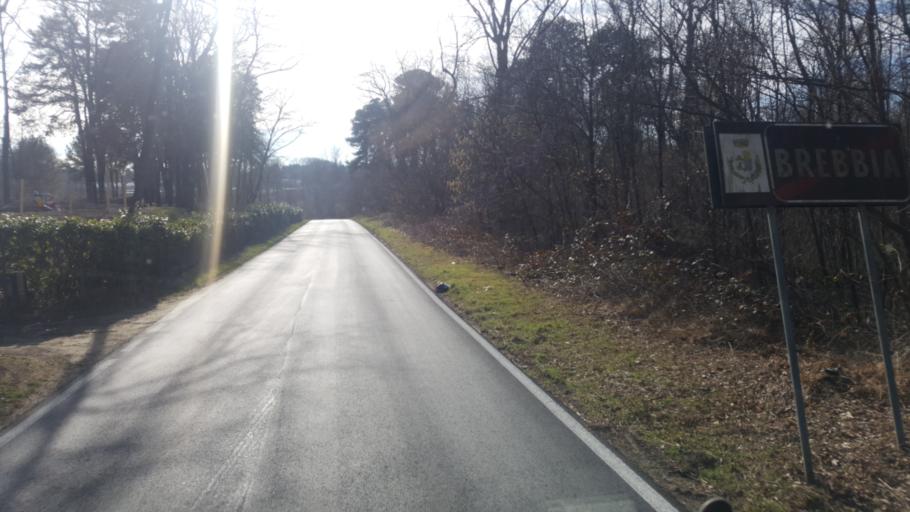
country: IT
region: Lombardy
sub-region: Provincia di Varese
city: Brebbia
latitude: 45.8158
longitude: 8.6432
